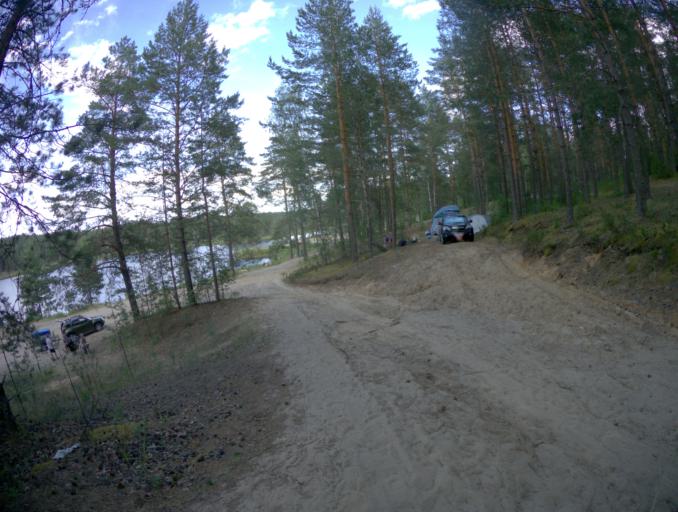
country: RU
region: Nizjnij Novgorod
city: Frolishchi
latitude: 56.3510
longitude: 42.7389
